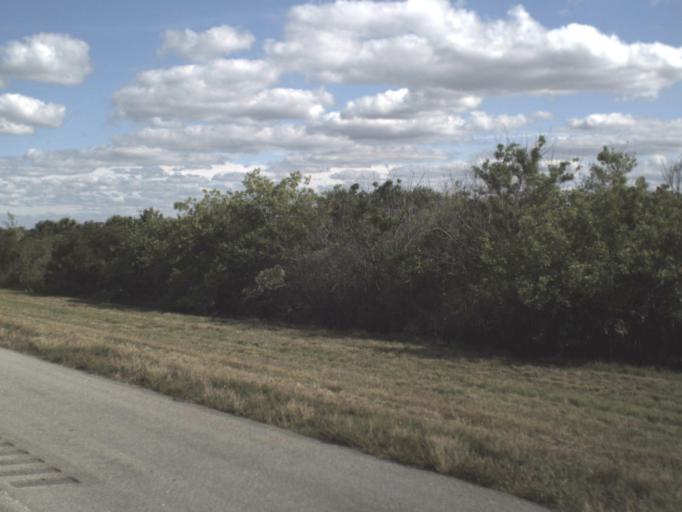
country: US
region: Florida
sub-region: Indian River County
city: Fellsmere
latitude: 27.5593
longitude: -80.7498
